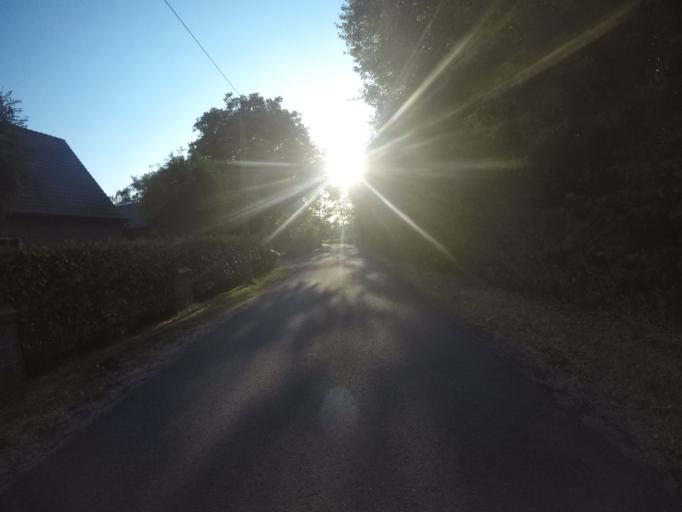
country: DE
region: North Rhine-Westphalia
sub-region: Regierungsbezirk Munster
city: Isselburg
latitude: 51.8662
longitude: 6.5271
